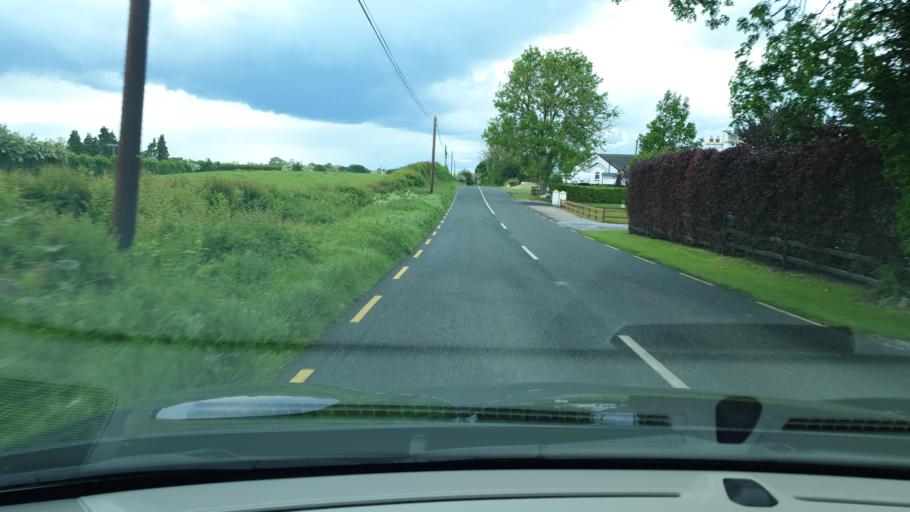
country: IE
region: Leinster
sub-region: Uibh Fhaili
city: Clara
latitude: 53.2340
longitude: -7.6359
